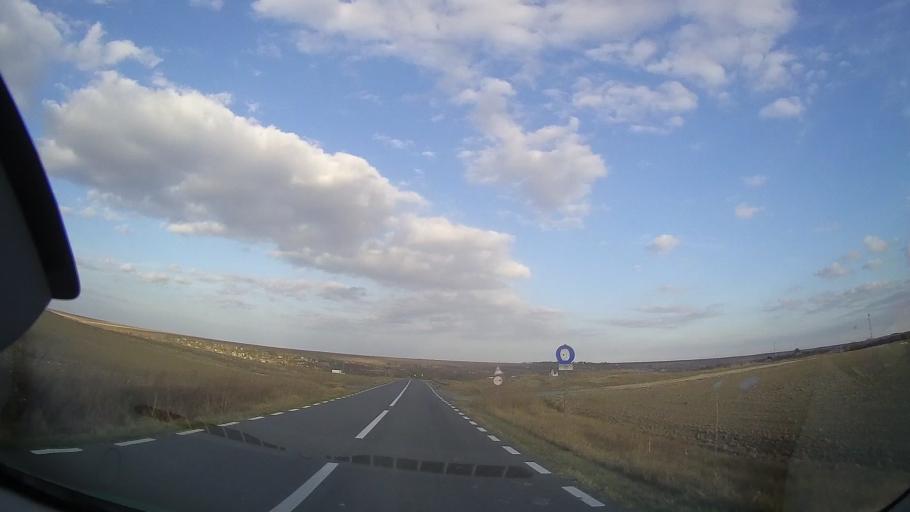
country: RO
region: Constanta
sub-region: Comuna Independenta
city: Independenta
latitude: 43.9481
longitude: 28.0716
